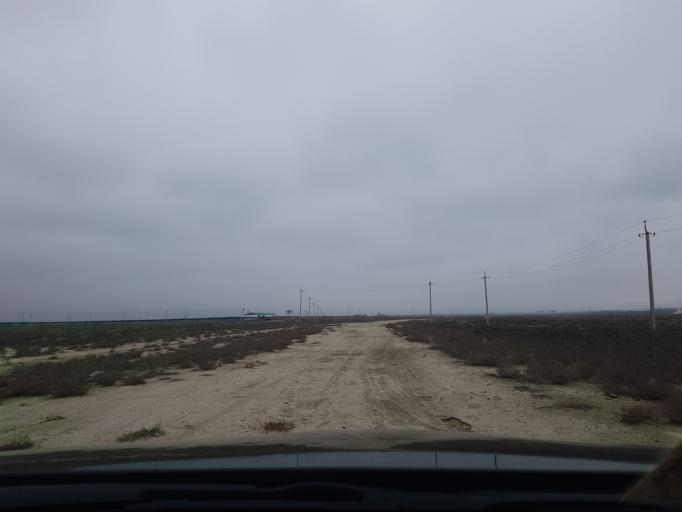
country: TM
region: Ahal
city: Abadan
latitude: 38.1426
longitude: 57.9797
